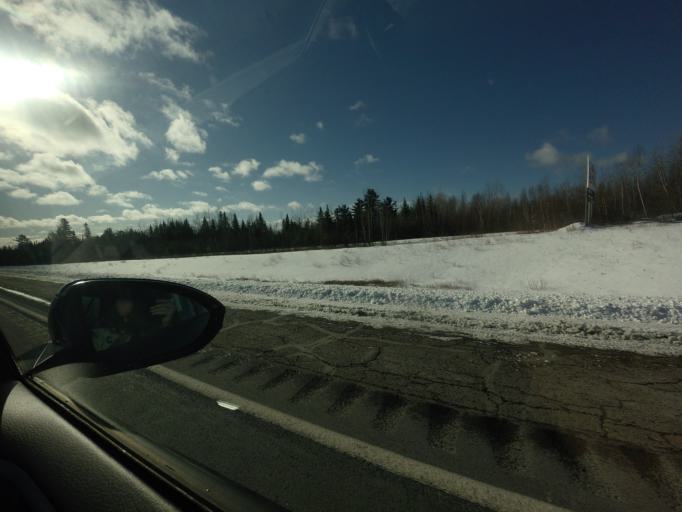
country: CA
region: New Brunswick
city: Fredericton
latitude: 45.8921
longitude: -66.6459
